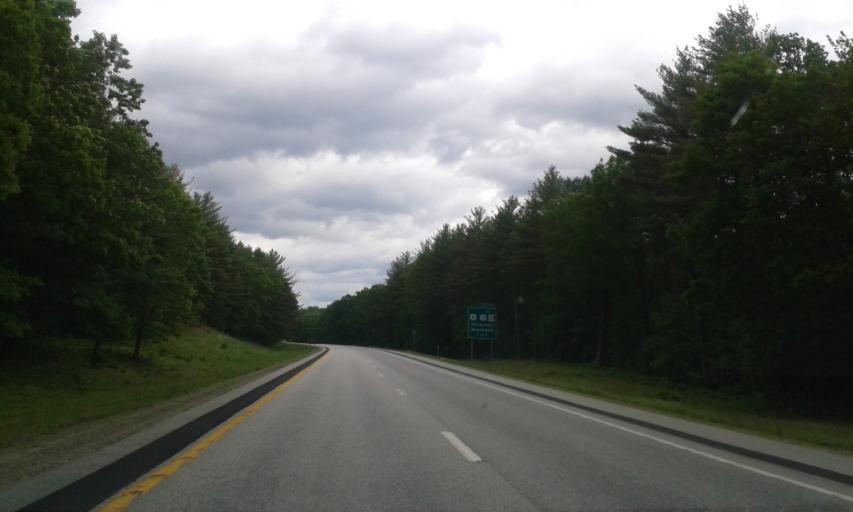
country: US
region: New Hampshire
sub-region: Merrimack County
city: Canterbury
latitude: 43.3083
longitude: -71.5856
